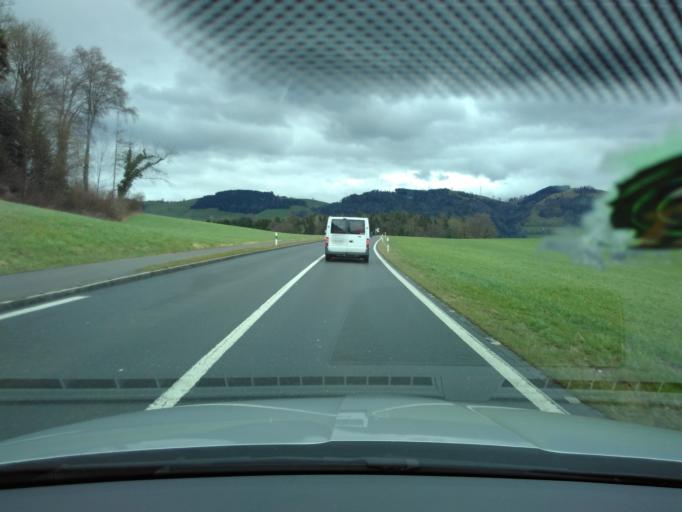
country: CH
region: Lucerne
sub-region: Hochdorf District
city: Inwil
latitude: 47.1227
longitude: 8.3660
